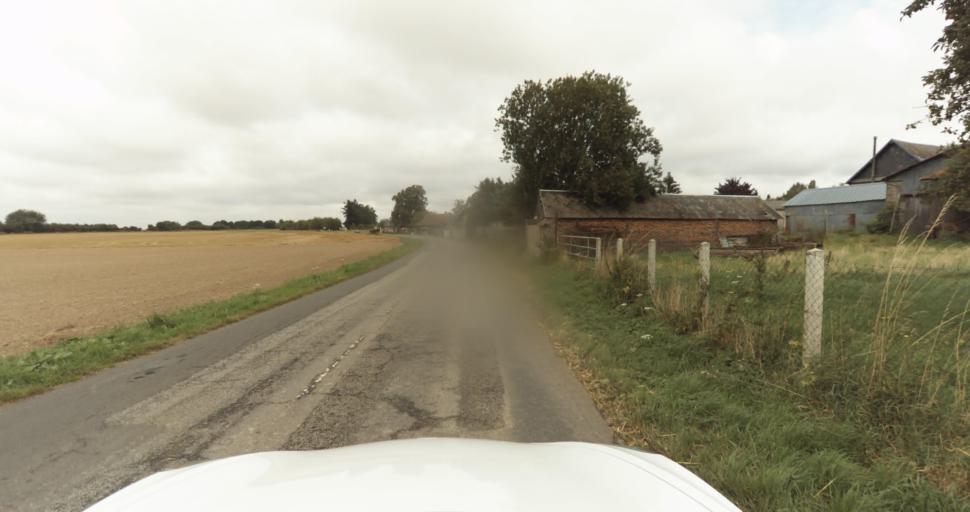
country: FR
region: Haute-Normandie
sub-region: Departement de l'Eure
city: Aviron
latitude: 49.0650
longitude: 1.0709
